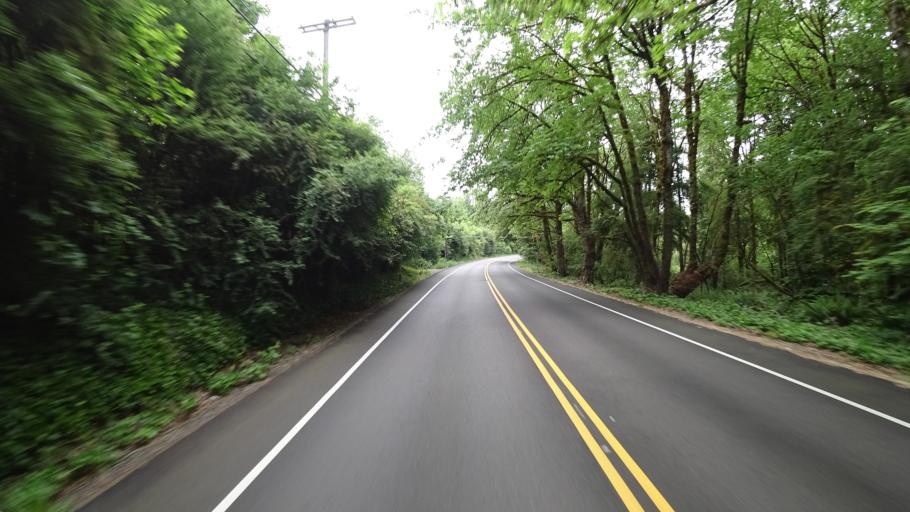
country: US
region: Oregon
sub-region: Clackamas County
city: Lake Oswego
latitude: 45.4399
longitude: -122.6696
